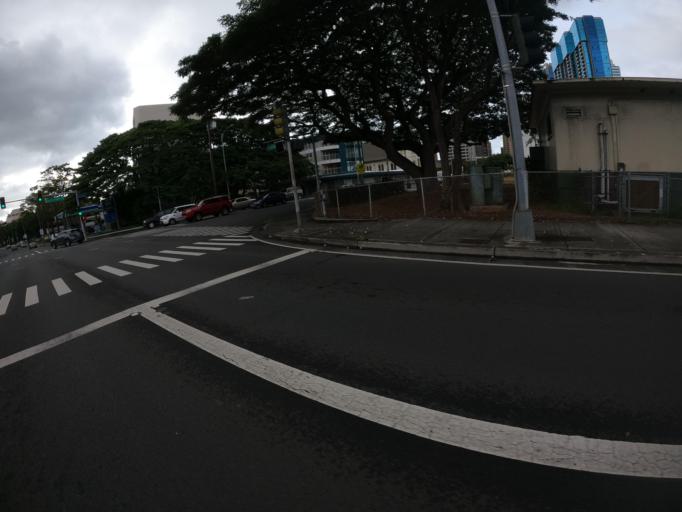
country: US
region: Hawaii
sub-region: Honolulu County
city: Honolulu
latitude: 21.3119
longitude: -157.8561
